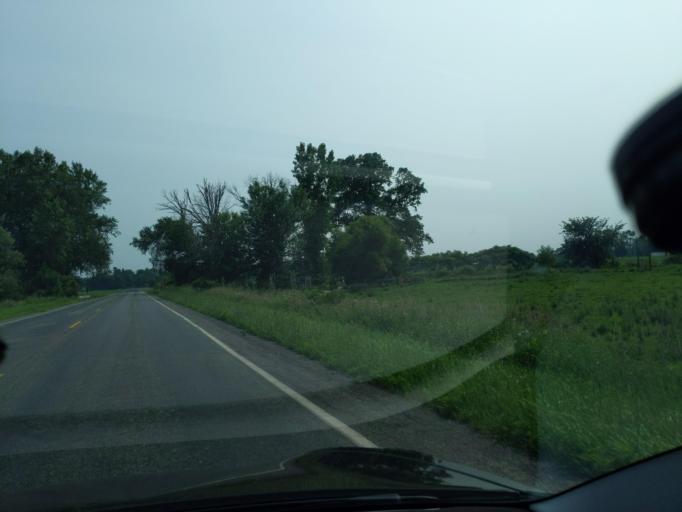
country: US
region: Michigan
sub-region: Eaton County
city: Eaton Rapids
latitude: 42.5019
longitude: -84.5612
